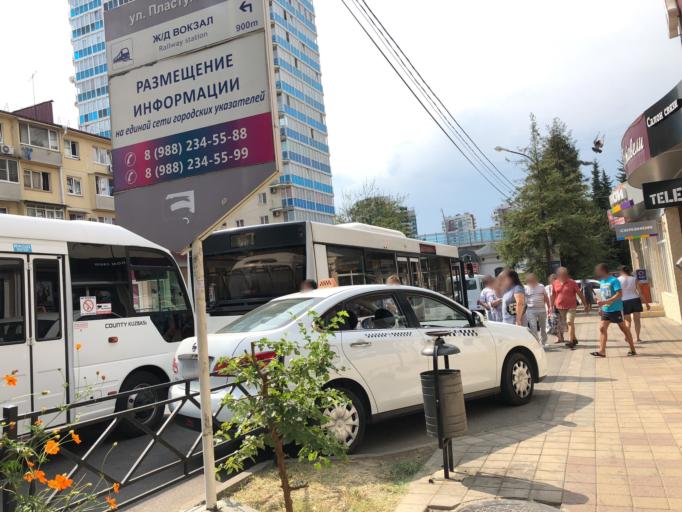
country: RU
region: Krasnodarskiy
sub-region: Sochi City
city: Sochi
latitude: 43.5963
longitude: 39.7337
